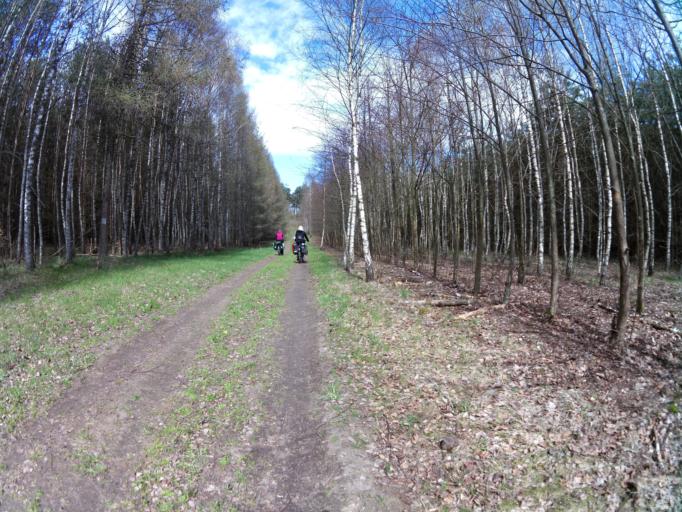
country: PL
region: West Pomeranian Voivodeship
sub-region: Powiat szczecinecki
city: Szczecinek
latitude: 53.7791
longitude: 16.6183
